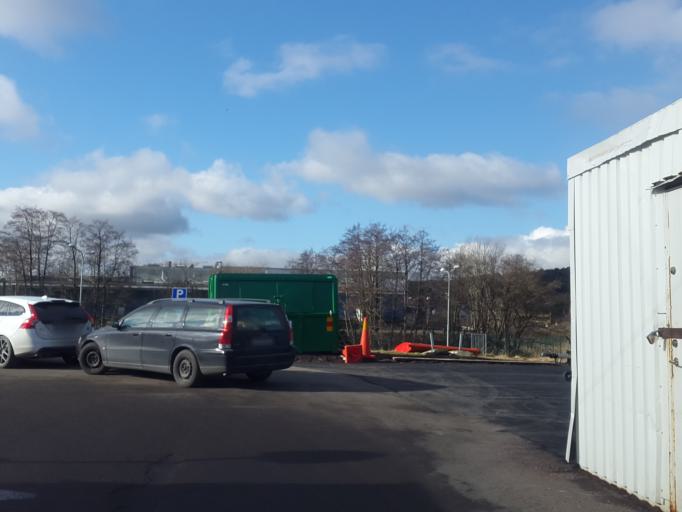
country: SE
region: Vaestra Goetaland
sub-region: Partille Kommun
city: Partille
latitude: 57.7415
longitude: 12.1239
